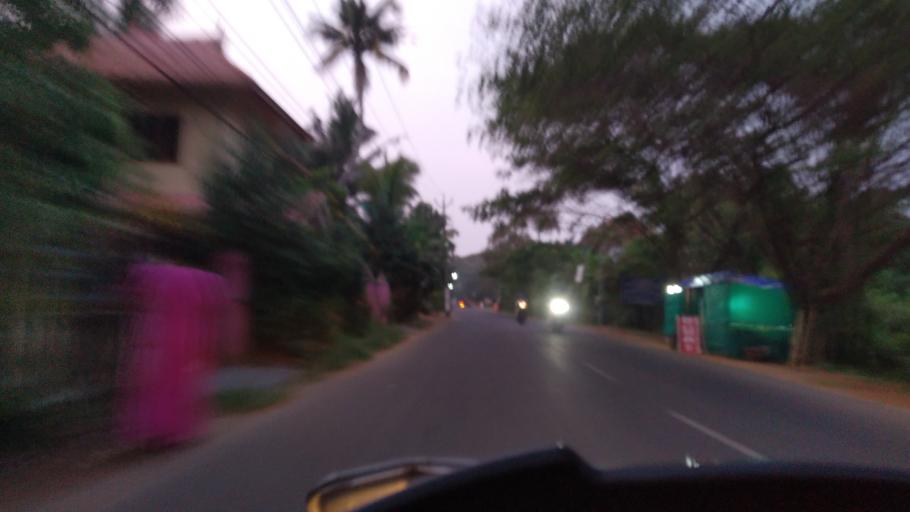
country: IN
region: Kerala
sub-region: Kottayam
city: Kottayam
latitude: 9.6130
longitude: 76.4334
